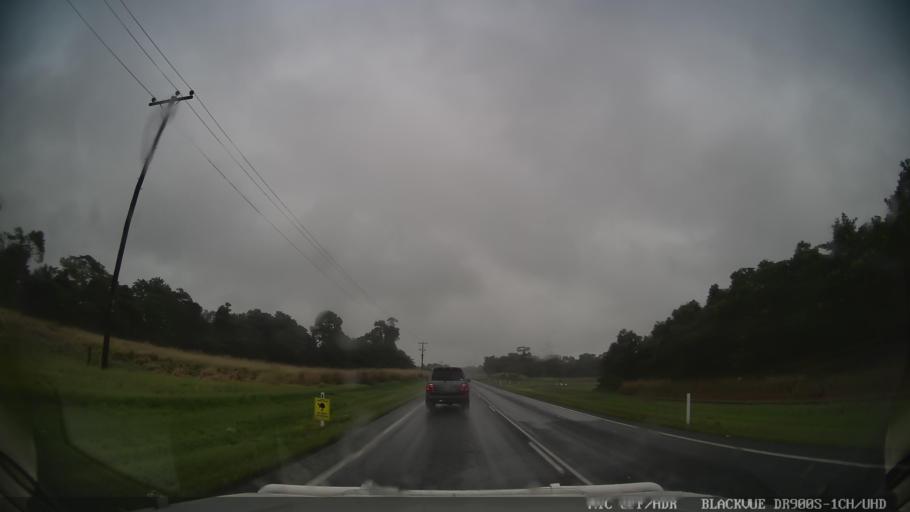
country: AU
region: Queensland
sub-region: Cassowary Coast
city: Innisfail
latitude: -17.6559
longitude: 146.0360
